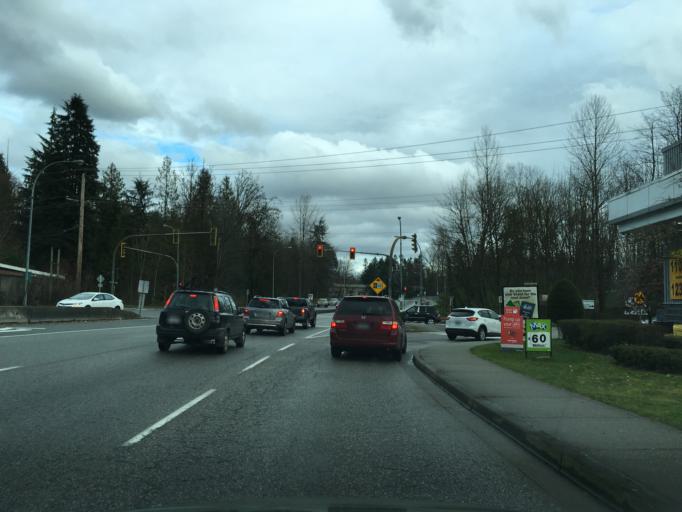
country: CA
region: British Columbia
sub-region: Fraser Valley Regional District
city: North Vancouver
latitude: 49.3120
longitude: -123.0221
